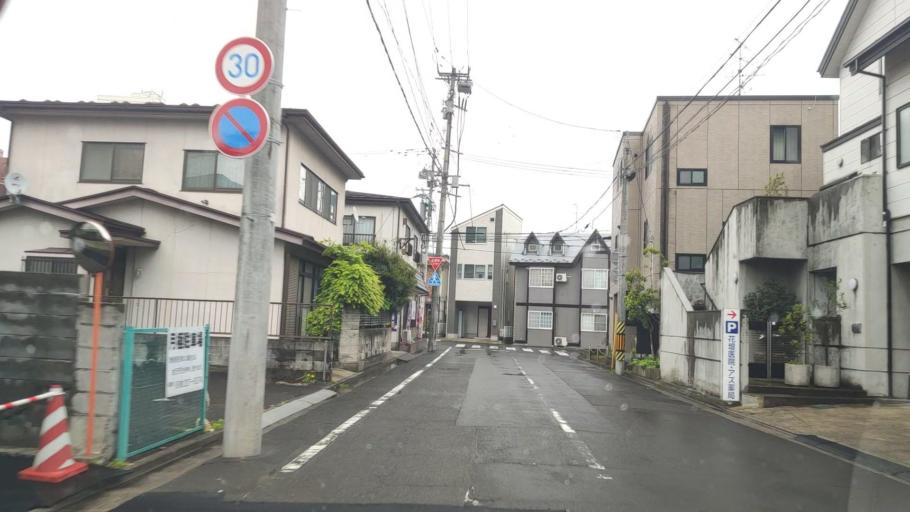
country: JP
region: Miyagi
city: Sendai
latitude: 38.2571
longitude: 140.8634
